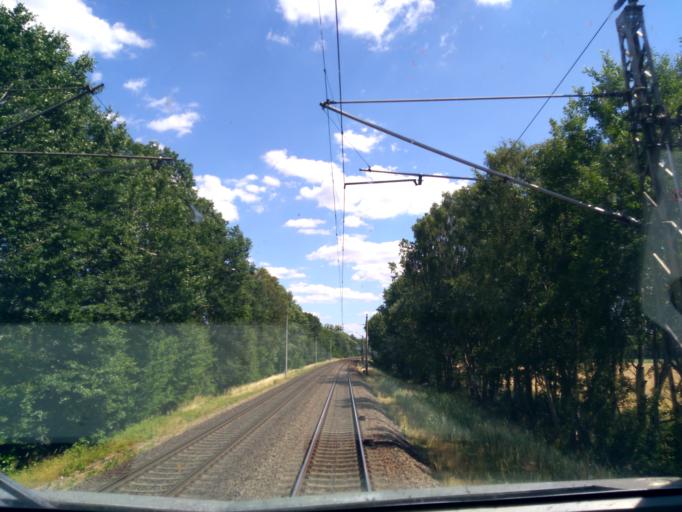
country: DE
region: Brandenburg
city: Bad Wilsnack
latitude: 52.9682
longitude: 11.9276
